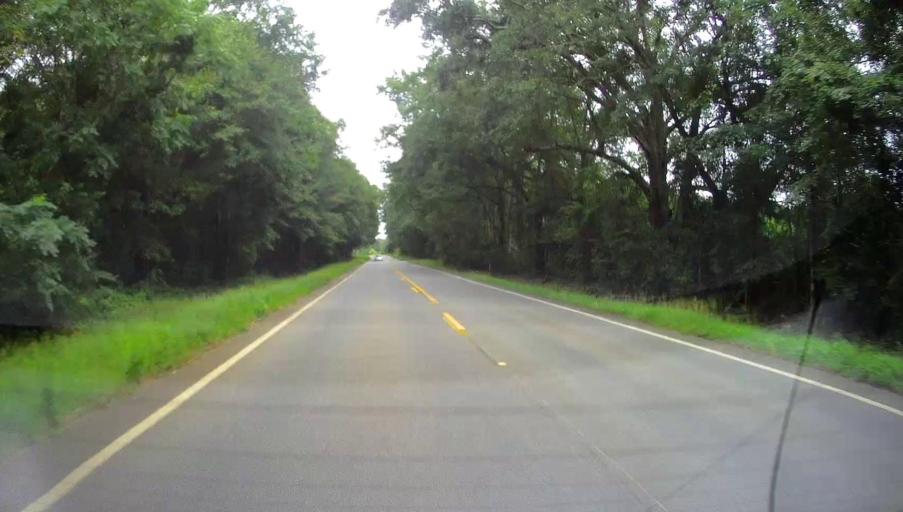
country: US
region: Georgia
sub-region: Schley County
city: Ellaville
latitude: 32.2542
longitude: -84.4034
